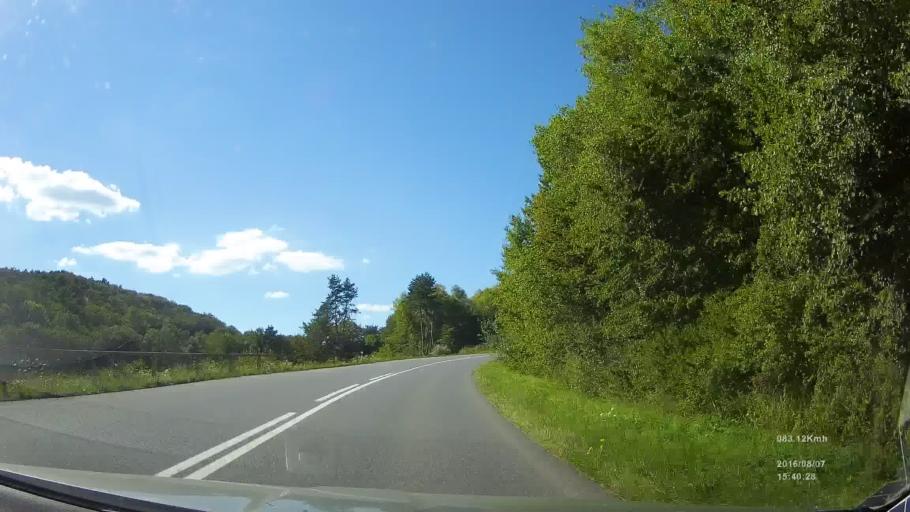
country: SK
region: Presovsky
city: Giraltovce
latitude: 49.1187
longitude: 21.5897
